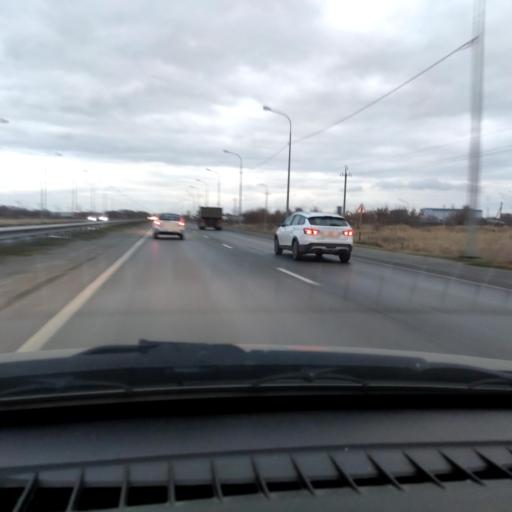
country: RU
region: Samara
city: Tol'yatti
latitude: 53.5752
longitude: 49.4396
